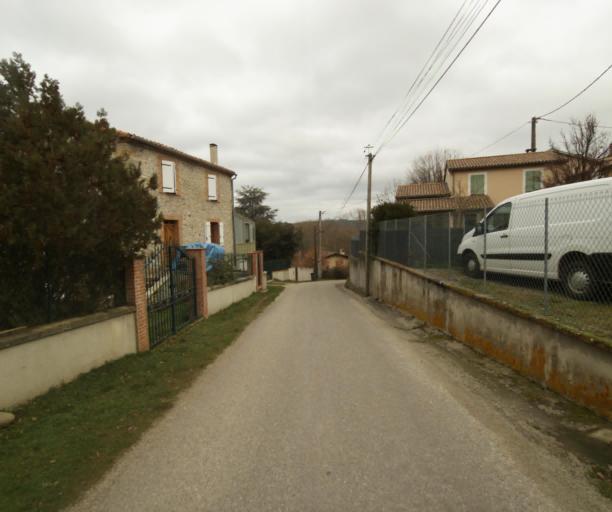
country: FR
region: Midi-Pyrenees
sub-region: Departement de l'Ariege
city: Pamiers
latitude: 43.1366
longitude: 1.6011
